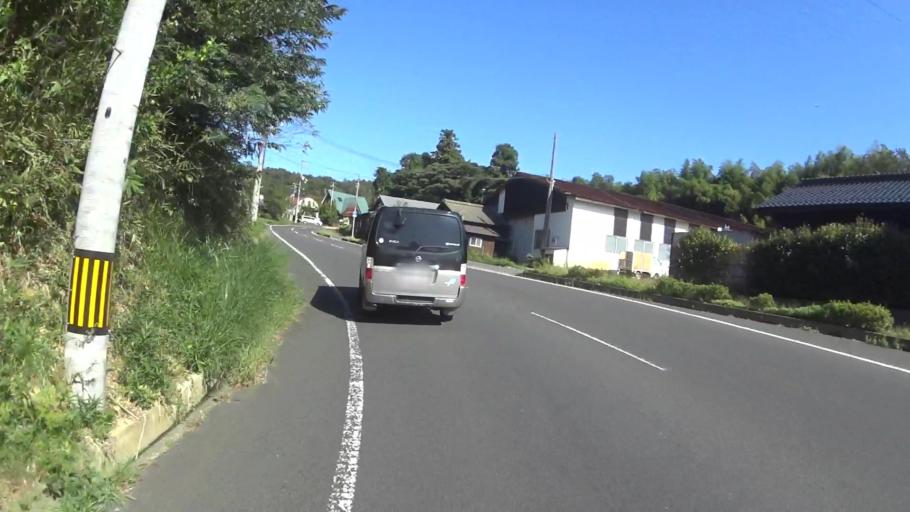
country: JP
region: Kyoto
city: Miyazu
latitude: 35.6941
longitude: 135.0461
